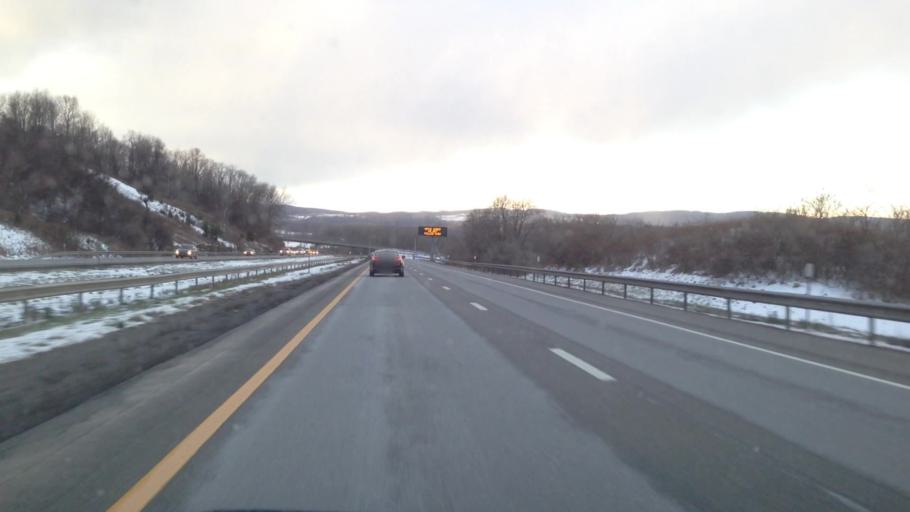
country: US
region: New York
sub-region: Herkimer County
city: Little Falls
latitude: 43.0119
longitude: -74.9187
